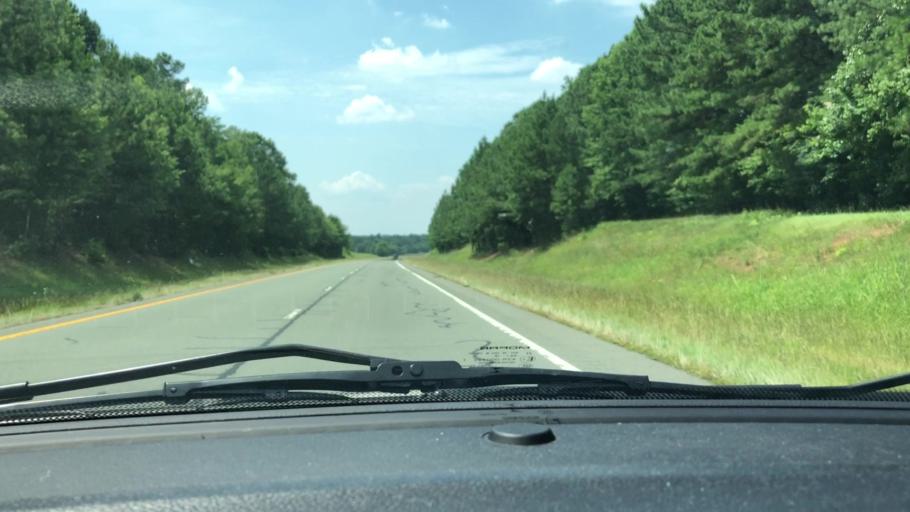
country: US
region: North Carolina
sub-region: Randolph County
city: Liberty
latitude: 35.7877
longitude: -79.5220
